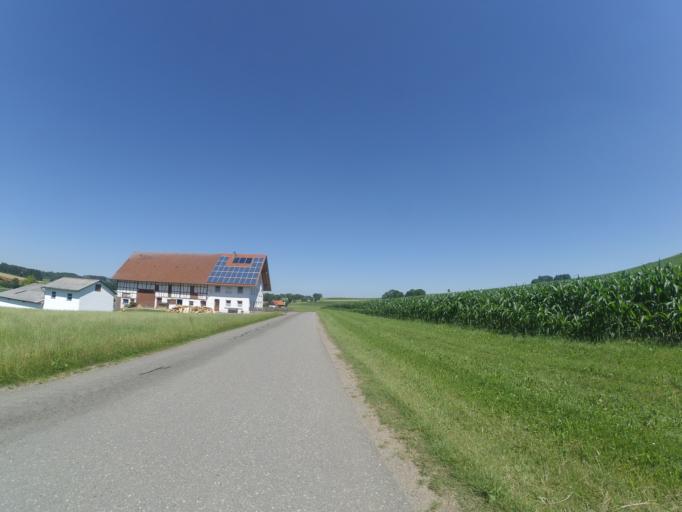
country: DE
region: Baden-Wuerttemberg
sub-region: Tuebingen Region
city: Bad Wurzach
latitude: 47.8881
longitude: 9.9120
